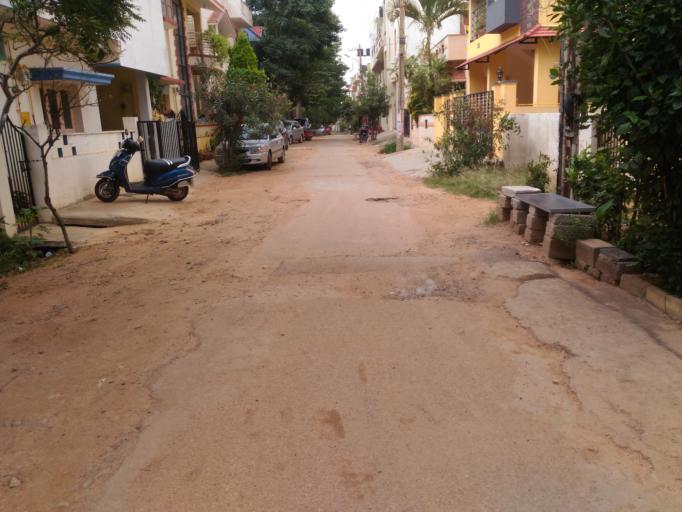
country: IN
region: Karnataka
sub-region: Bangalore Urban
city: Bangalore
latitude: 12.8714
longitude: 77.6452
